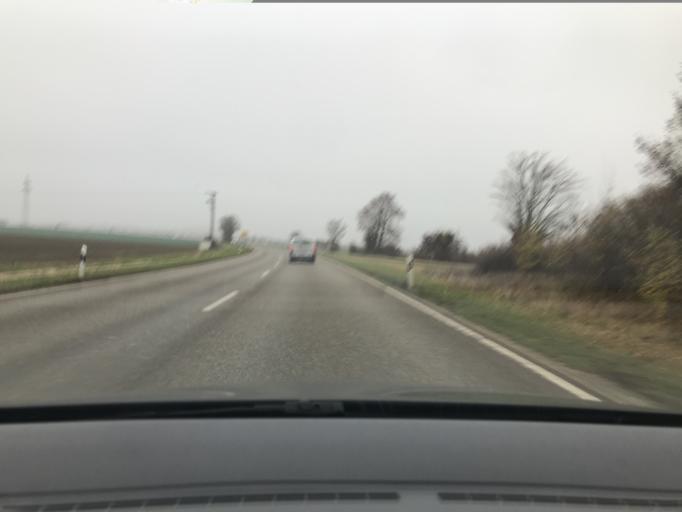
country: DE
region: Bavaria
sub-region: Swabia
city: Noerdlingen
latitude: 48.8640
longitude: 10.4720
